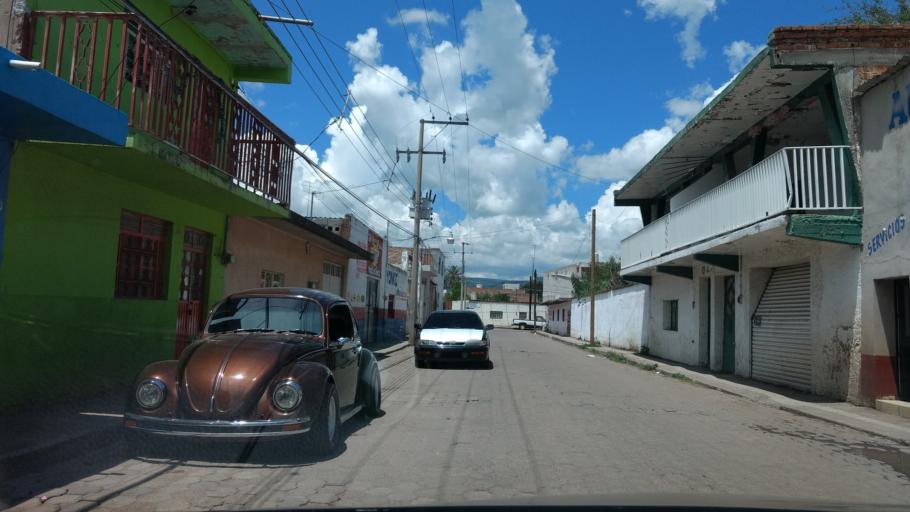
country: MX
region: Zacatecas
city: Tlaltenango de Sanchez Roman
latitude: 21.7785
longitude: -103.3037
